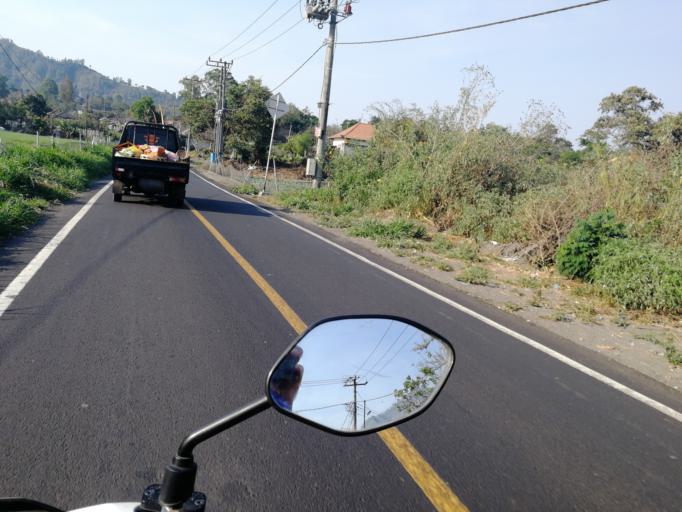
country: ID
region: Bali
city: Banjar Trunyan
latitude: -8.2399
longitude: 115.4066
